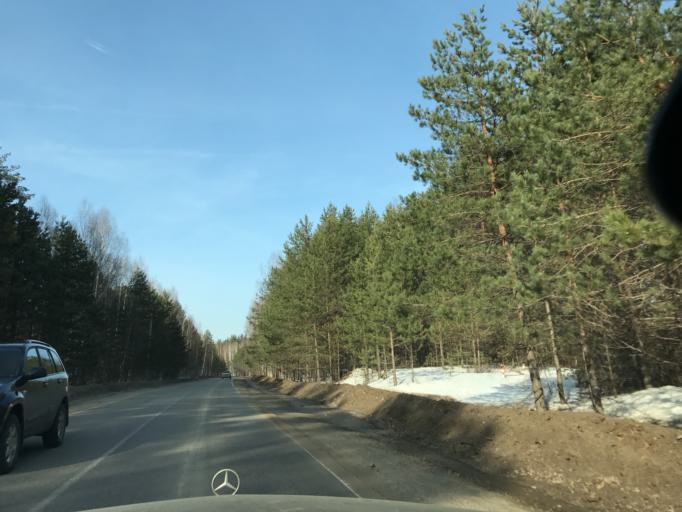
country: RU
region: Vladimir
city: Galitsy
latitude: 56.0042
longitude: 42.8599
